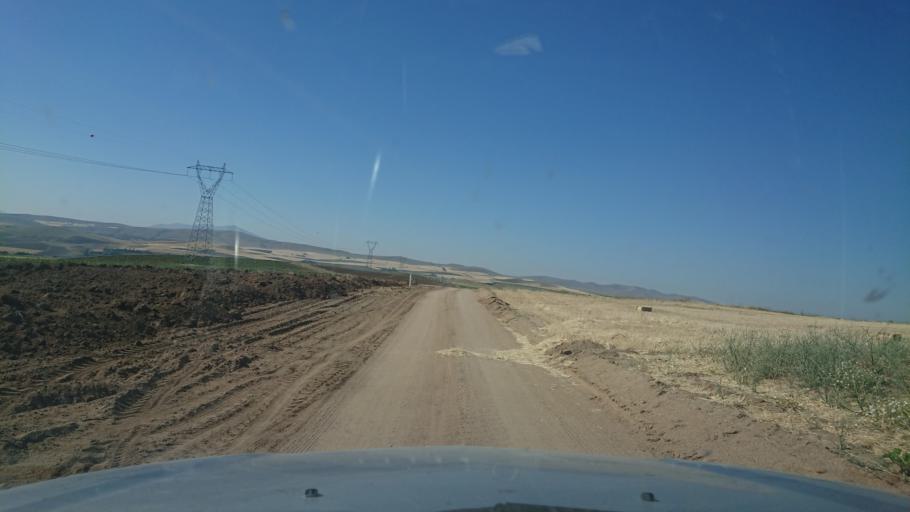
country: TR
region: Aksaray
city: Agacoren
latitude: 38.8386
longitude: 33.9443
